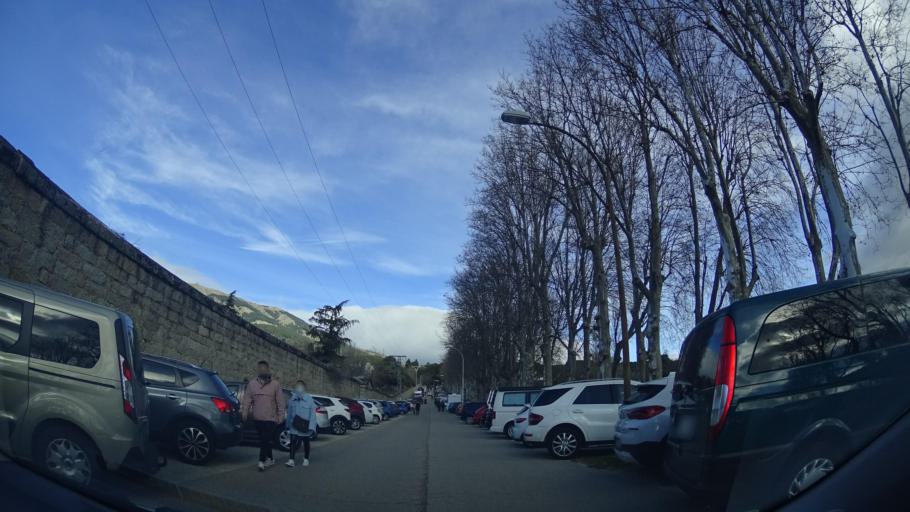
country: ES
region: Madrid
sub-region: Provincia de Madrid
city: San Lorenzo de El Escorial
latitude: 40.5864
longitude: -4.1441
